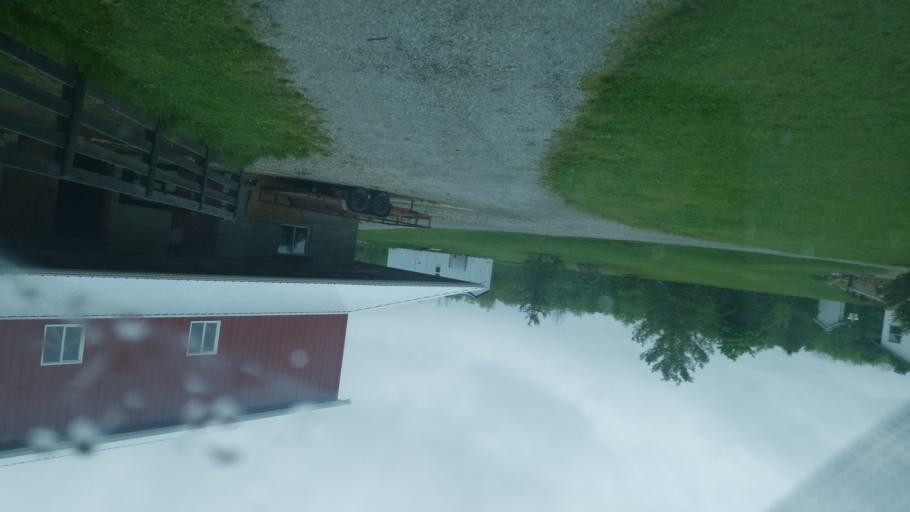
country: US
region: Ohio
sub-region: Highland County
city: Leesburg
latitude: 39.2590
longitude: -83.5410
